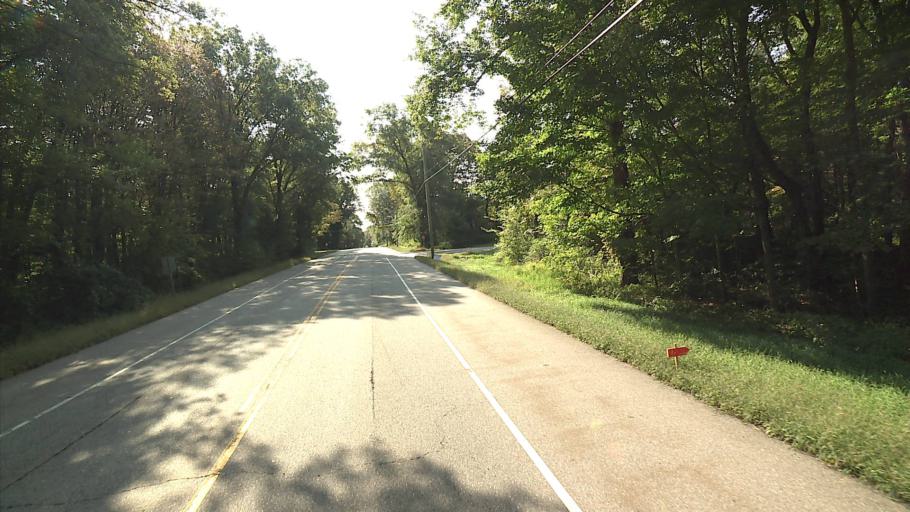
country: US
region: Connecticut
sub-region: New London County
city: Baltic
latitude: 41.5887
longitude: -72.1579
